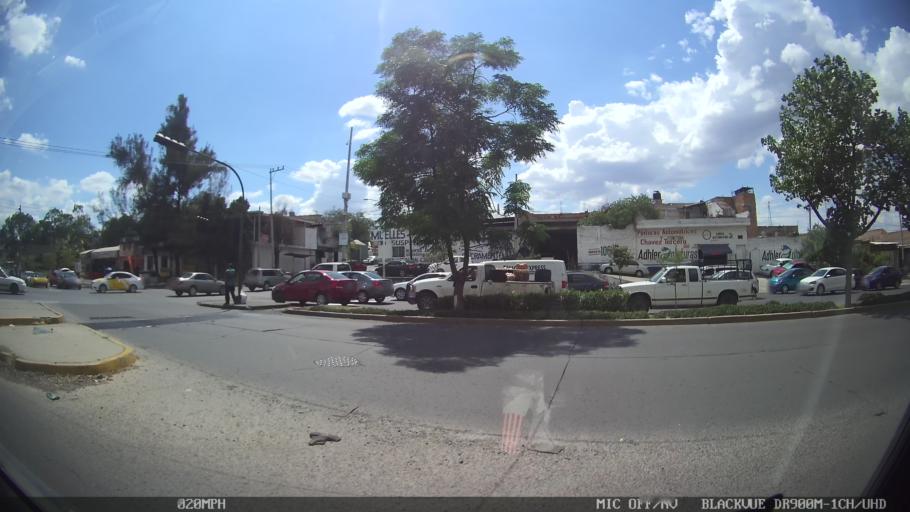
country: MX
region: Jalisco
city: Tlaquepaque
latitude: 20.6785
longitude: -103.2670
